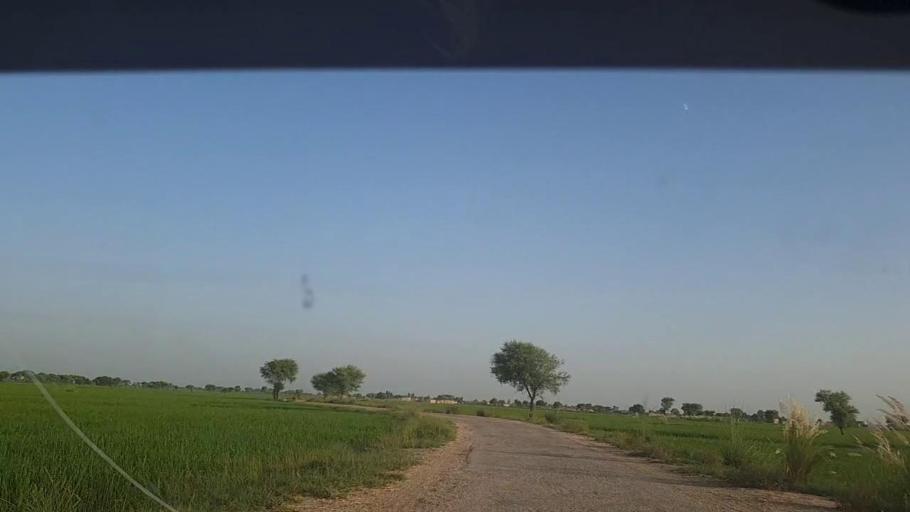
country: PK
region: Sindh
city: Thul
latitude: 28.1363
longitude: 68.8876
